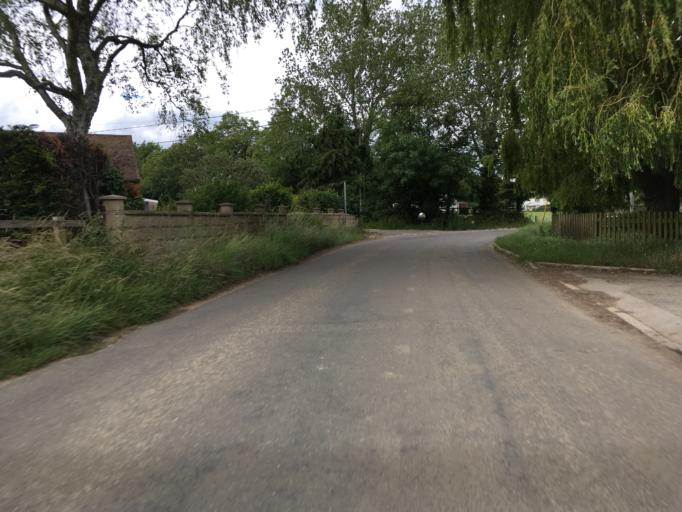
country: GB
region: England
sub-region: Oxfordshire
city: Boars Hill
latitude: 51.6997
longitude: -1.2885
